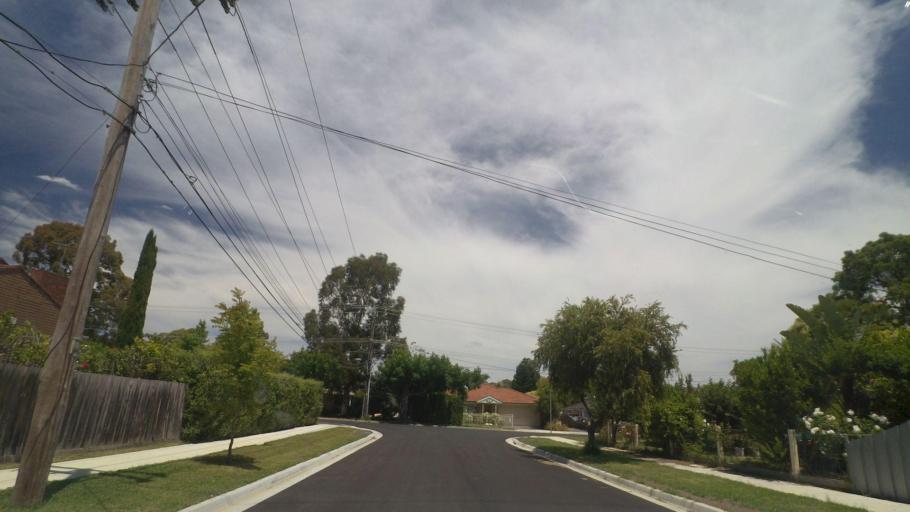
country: AU
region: Victoria
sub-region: Knox
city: Boronia
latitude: -37.8561
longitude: 145.2934
